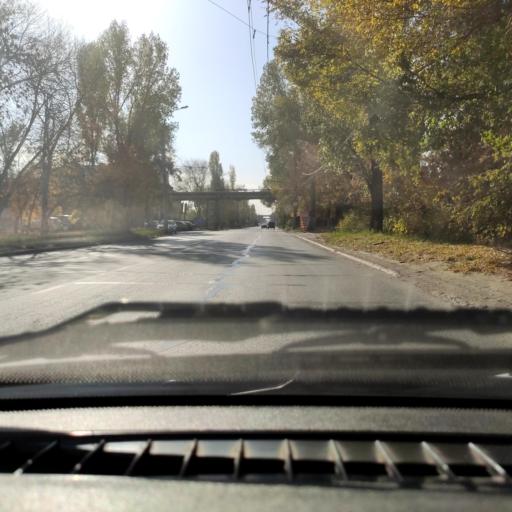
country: RU
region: Samara
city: Tol'yatti
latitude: 53.5498
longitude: 49.4482
